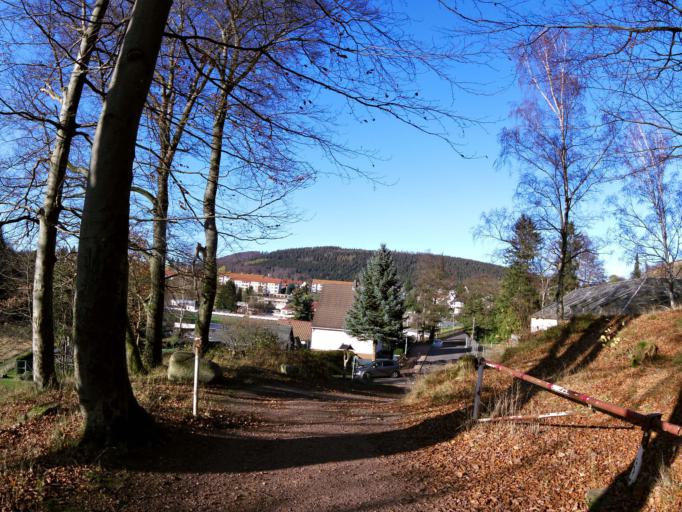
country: DE
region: Thuringia
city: Ruhla
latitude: 50.8792
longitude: 10.3884
